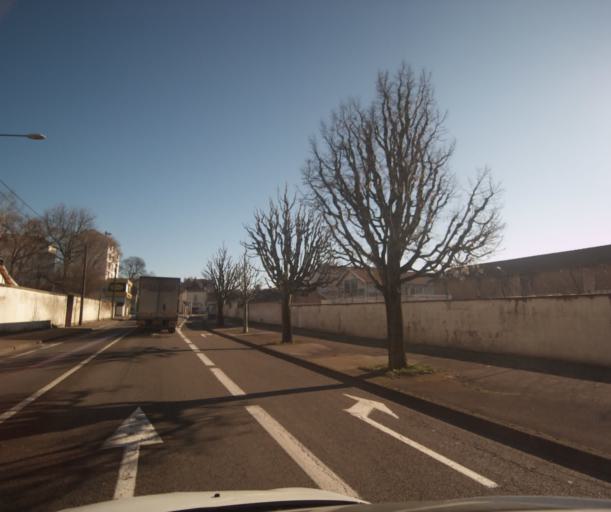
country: FR
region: Franche-Comte
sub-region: Departement du Doubs
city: Besancon
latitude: 47.2335
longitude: 6.0057
